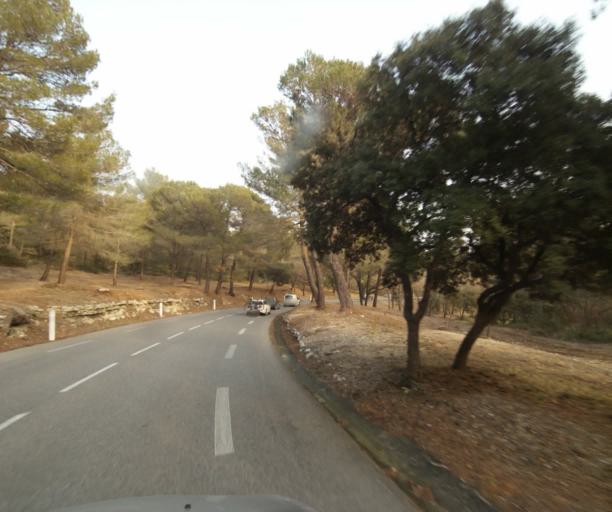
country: FR
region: Provence-Alpes-Cote d'Azur
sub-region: Departement des Bouches-du-Rhone
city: Rognes
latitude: 43.6223
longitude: 5.3535
